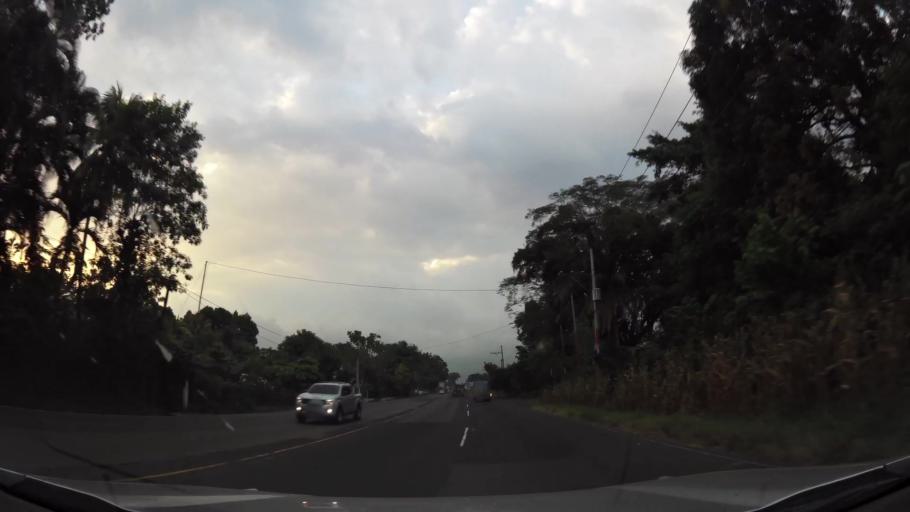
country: GT
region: Escuintla
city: Siquinala
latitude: 14.2928
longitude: -90.9423
